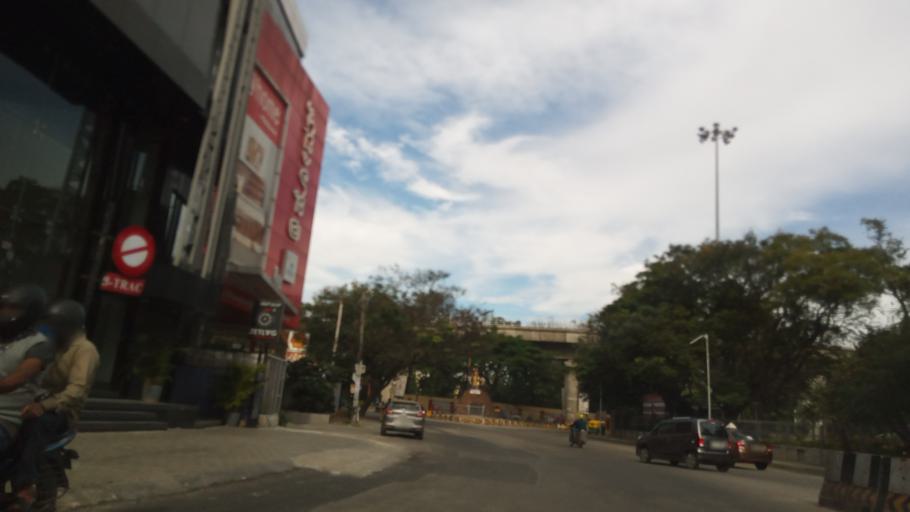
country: IN
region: Karnataka
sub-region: Bangalore Urban
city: Bangalore
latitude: 13.0122
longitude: 77.5543
